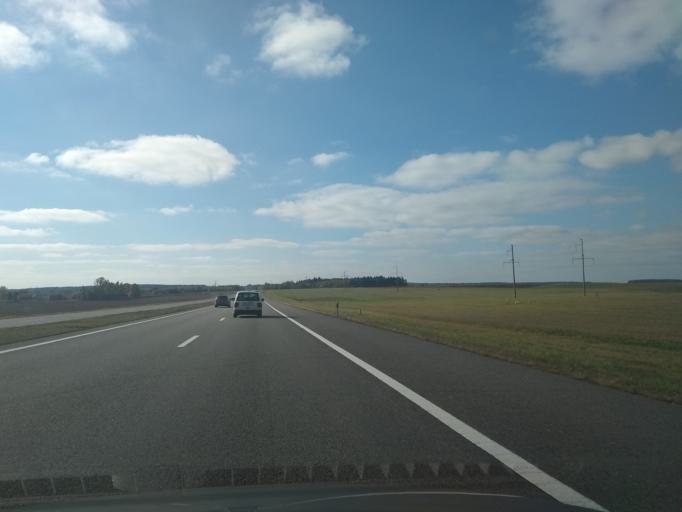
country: BY
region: Minsk
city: Haradzyeya
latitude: 53.3948
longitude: 26.5340
